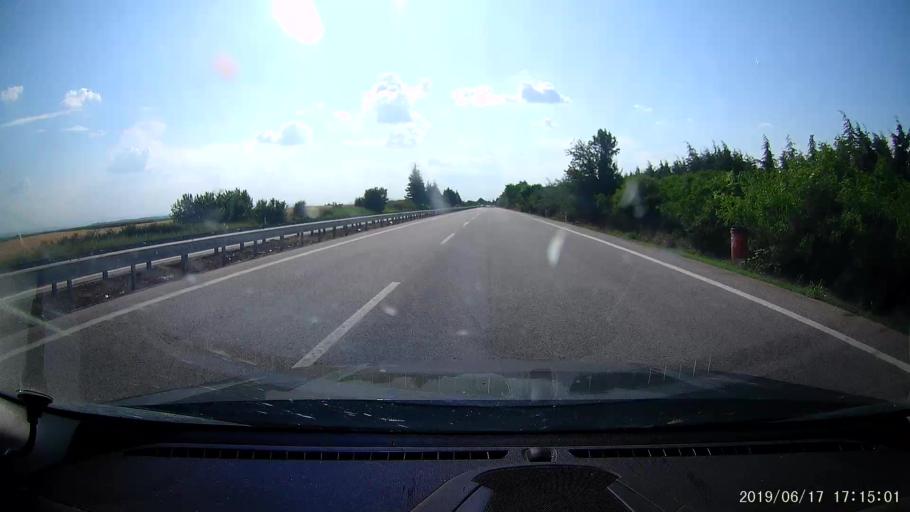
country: TR
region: Edirne
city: Edirne
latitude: 41.7004
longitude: 26.5057
